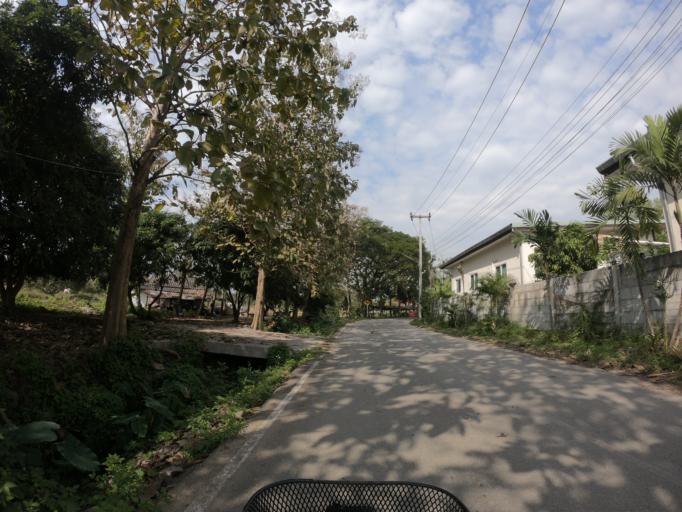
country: TH
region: Chiang Mai
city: Saraphi
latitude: 18.7418
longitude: 99.0607
